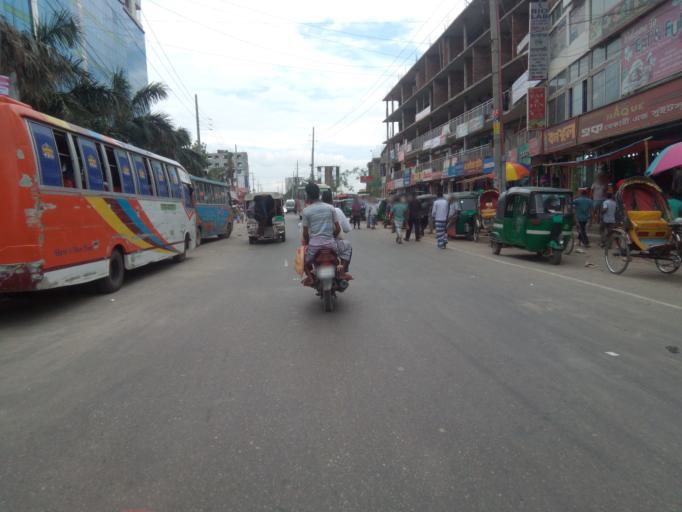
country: BD
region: Dhaka
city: Paltan
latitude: 23.7200
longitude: 90.4905
